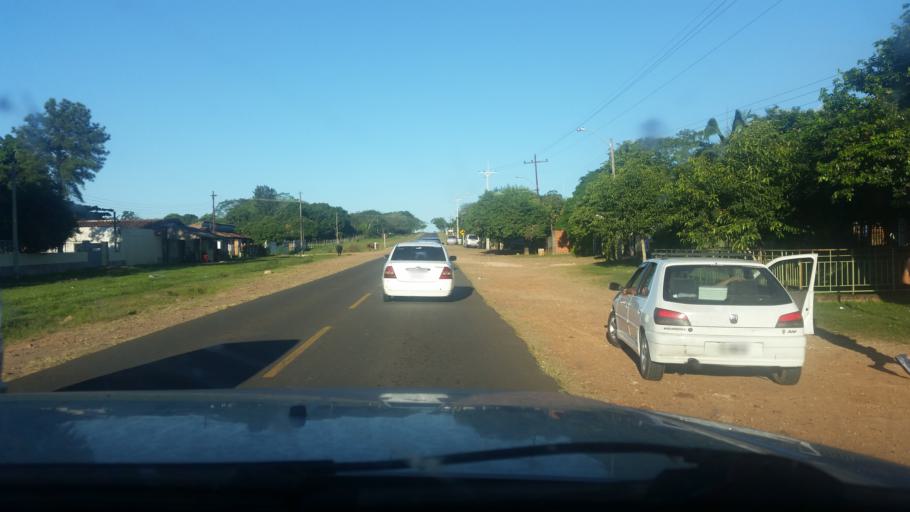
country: PY
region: Guaira
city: Independencia
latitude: -25.7230
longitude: -56.3198
